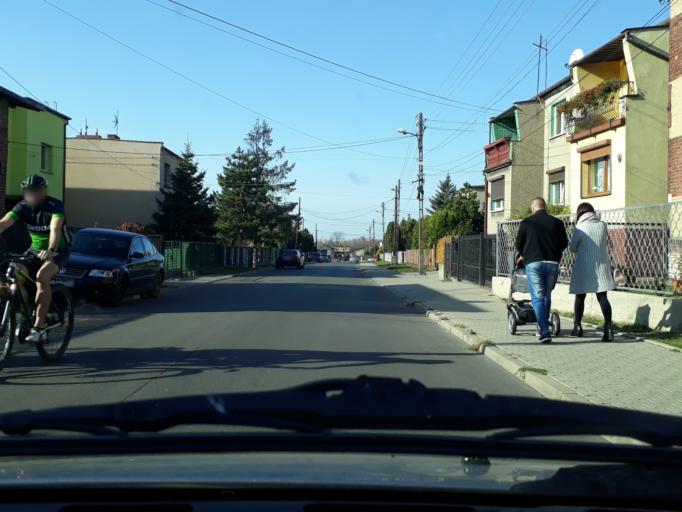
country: PL
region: Silesian Voivodeship
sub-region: Powiat tarnogorski
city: Radzionkow
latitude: 50.4216
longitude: 18.8813
